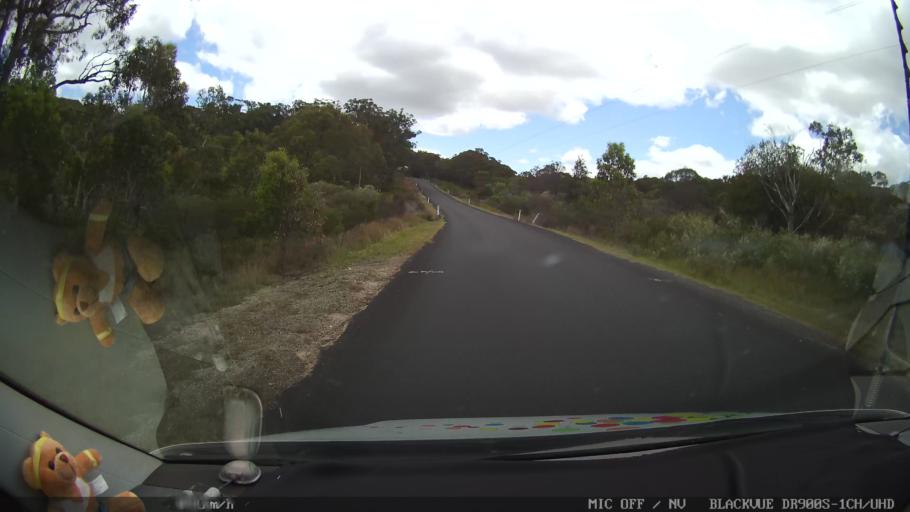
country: AU
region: New South Wales
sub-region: Glen Innes Severn
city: Glen Innes
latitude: -29.4377
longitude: 151.6286
